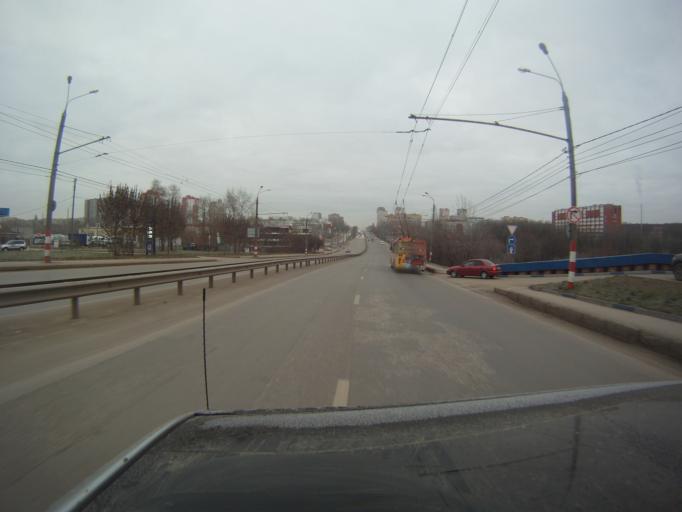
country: RU
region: Nizjnij Novgorod
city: Nizhniy Novgorod
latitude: 56.2905
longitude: 44.0361
